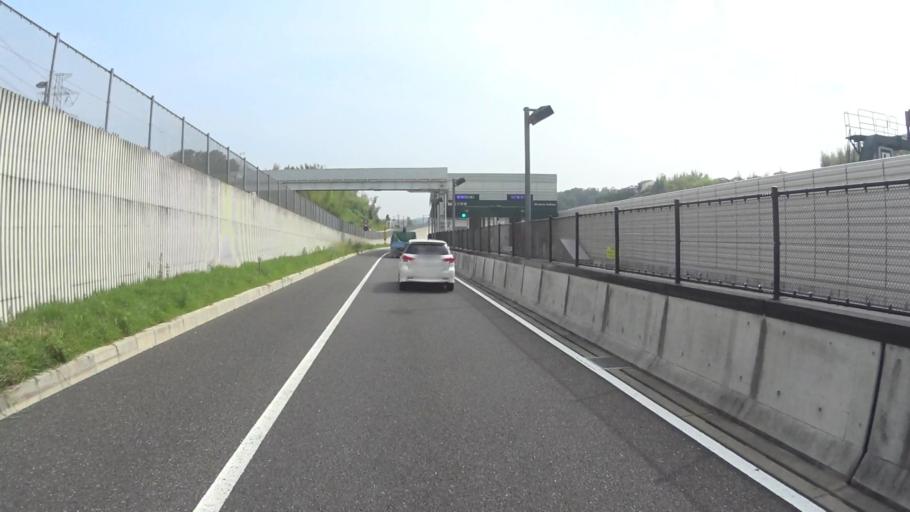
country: JP
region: Kyoto
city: Tanabe
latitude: 34.8071
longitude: 135.7103
